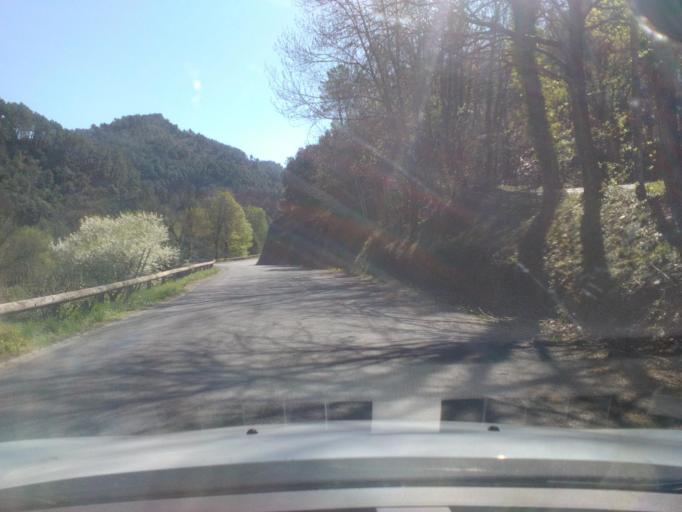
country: FR
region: Languedoc-Roussillon
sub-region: Departement du Gard
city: Valleraugue
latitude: 44.1782
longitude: 3.7442
